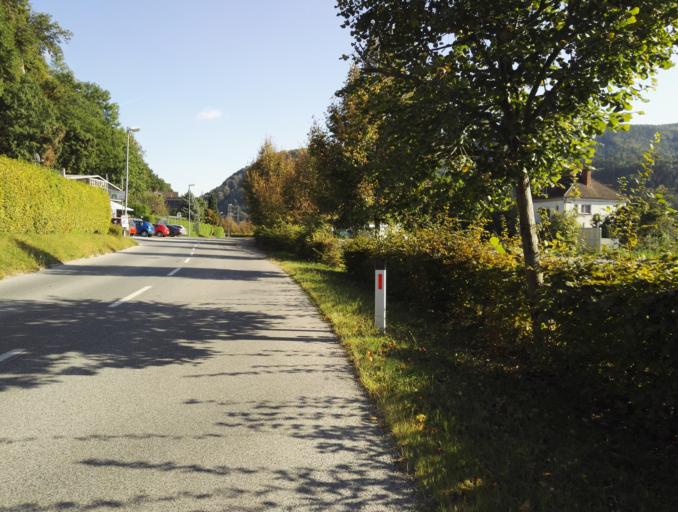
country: AT
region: Styria
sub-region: Politischer Bezirk Graz-Umgebung
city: Gratkorn
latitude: 47.1247
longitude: 15.3526
